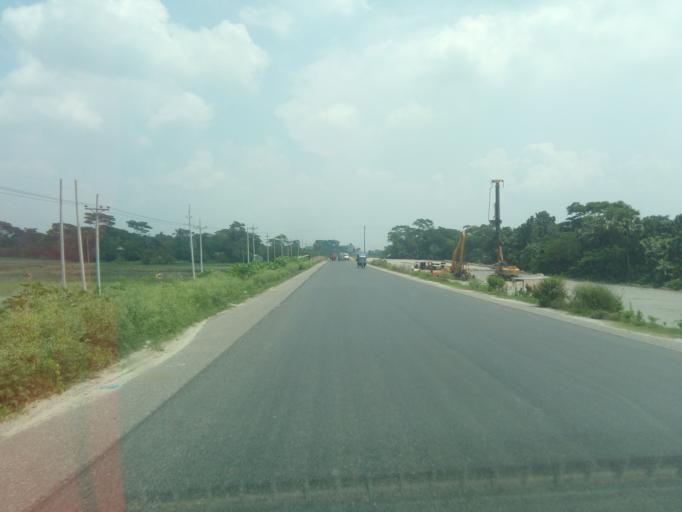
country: BD
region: Dhaka
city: Char Bhadrasan
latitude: 23.3757
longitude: 90.0217
